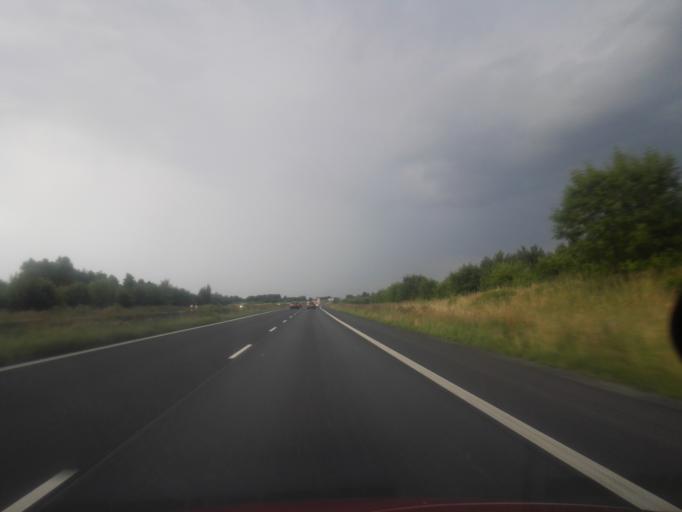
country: PL
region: Silesian Voivodeship
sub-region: Powiat czestochowski
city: Borowno
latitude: 50.9468
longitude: 19.2397
